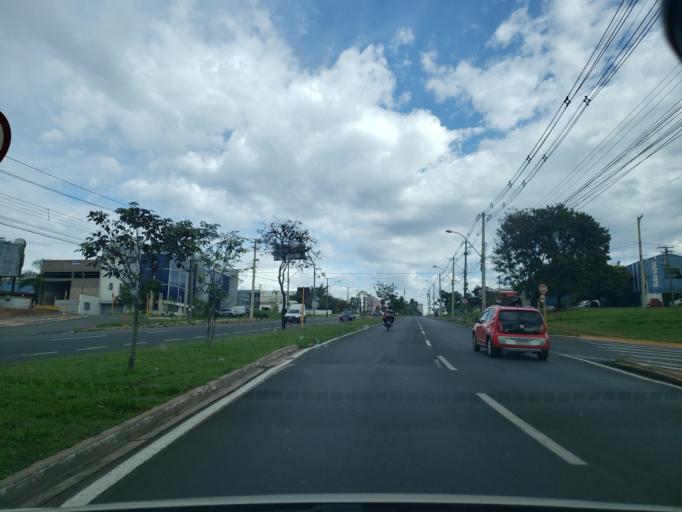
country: BR
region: Sao Paulo
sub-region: Bauru
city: Bauru
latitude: -22.3378
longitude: -49.0415
